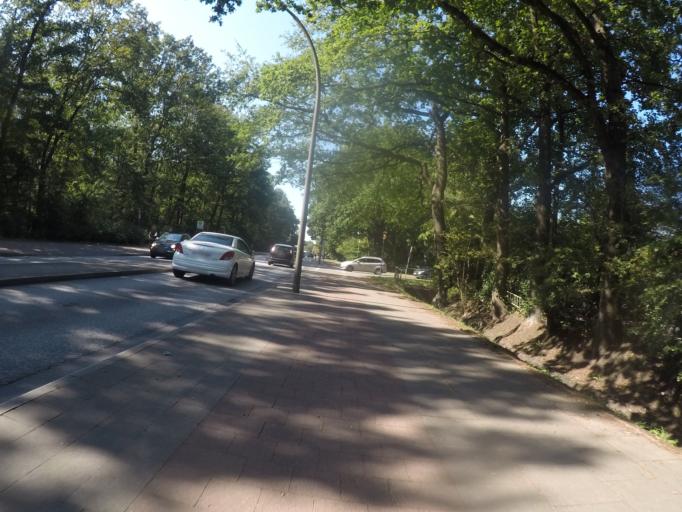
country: DE
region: Hamburg
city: Langenhorn
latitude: 53.6490
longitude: 9.9929
